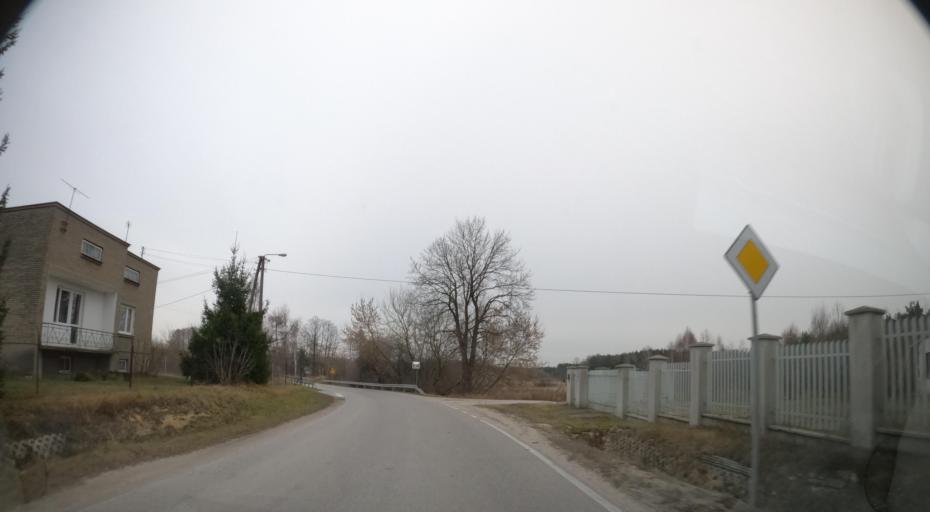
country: PL
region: Masovian Voivodeship
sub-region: Powiat radomski
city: Jastrzebia
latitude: 51.4892
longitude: 21.1746
